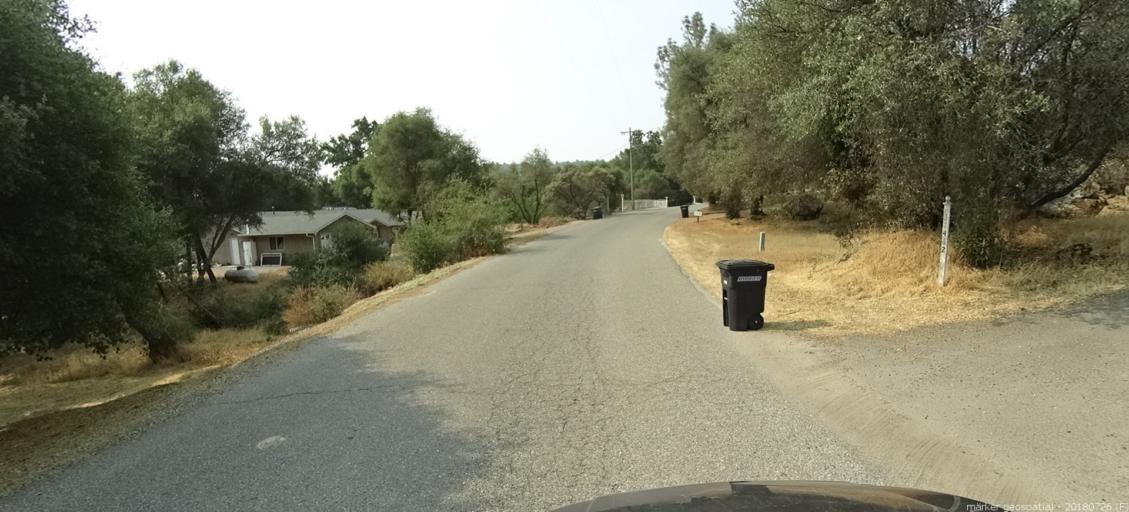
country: US
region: California
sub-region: Madera County
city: Coarsegold
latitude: 37.2061
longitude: -119.6844
